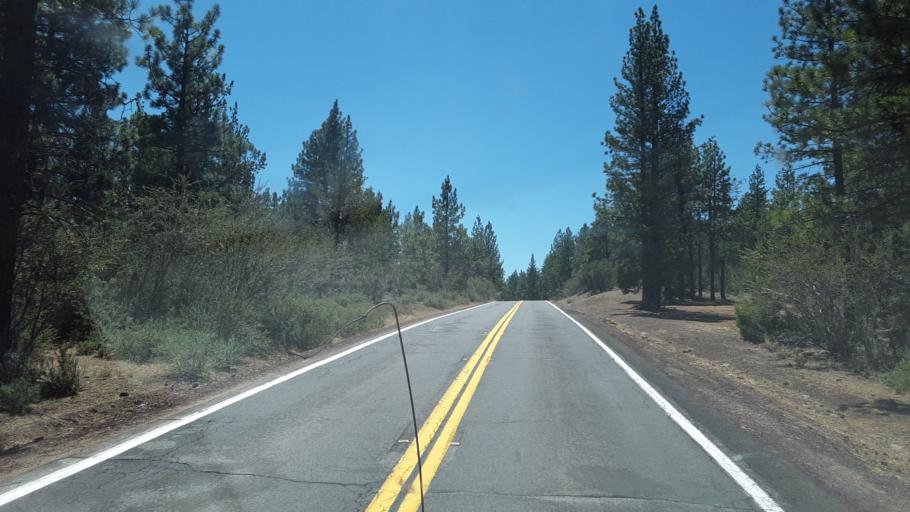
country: US
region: California
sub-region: Lassen County
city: Johnstonville
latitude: 40.4777
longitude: -120.5501
